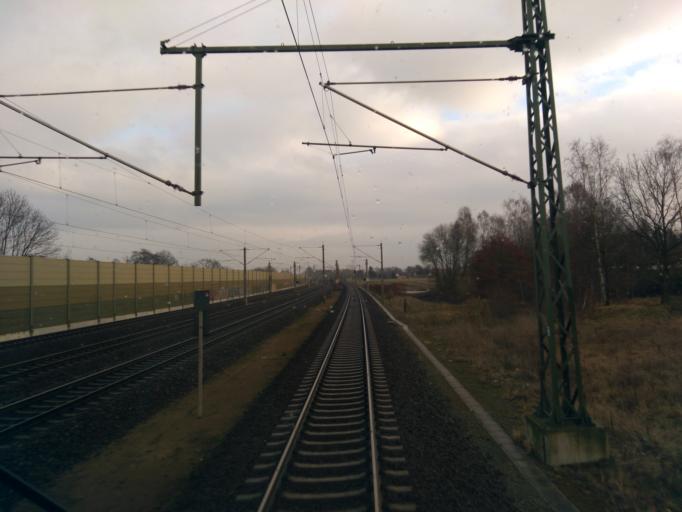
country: DE
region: Lower Saxony
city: Stelle
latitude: 53.3732
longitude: 10.1326
